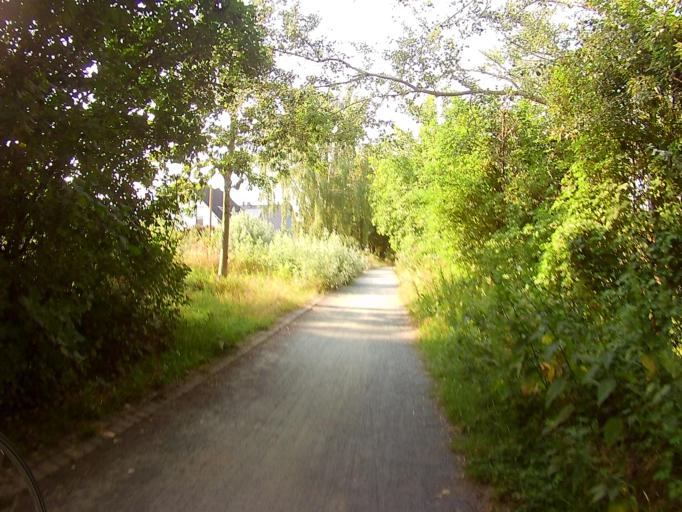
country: DE
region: Berlin
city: Biesdorf
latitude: 52.4949
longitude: 13.5680
